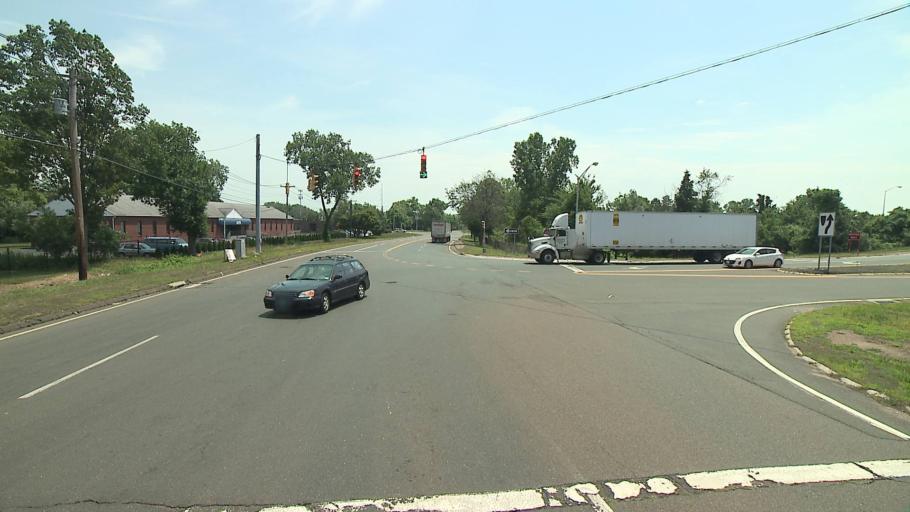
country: US
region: Connecticut
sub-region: New Haven County
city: Hamden
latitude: 41.3804
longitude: -72.8807
